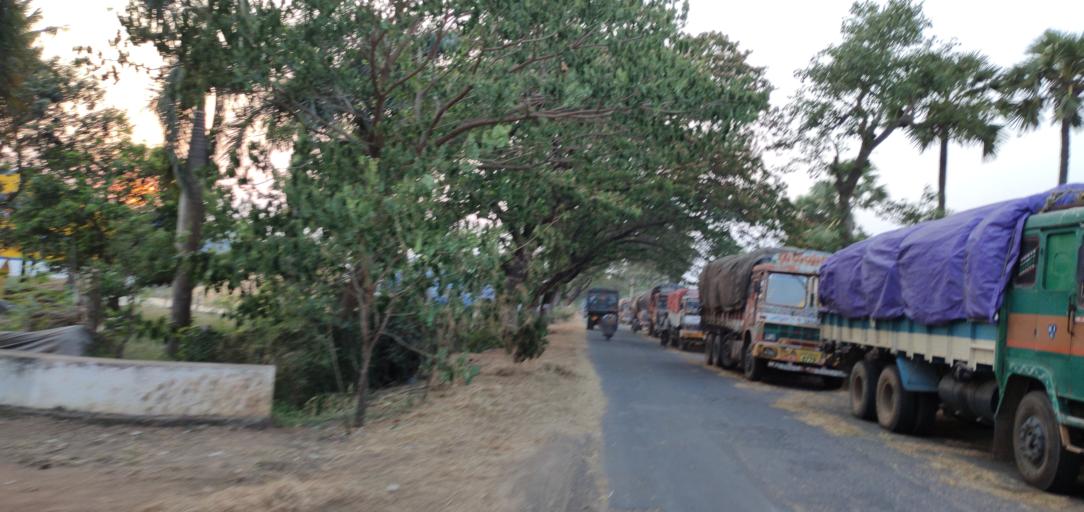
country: IN
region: Andhra Pradesh
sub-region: West Godavari
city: Tadepallegudem
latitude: 16.8471
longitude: 81.4908
